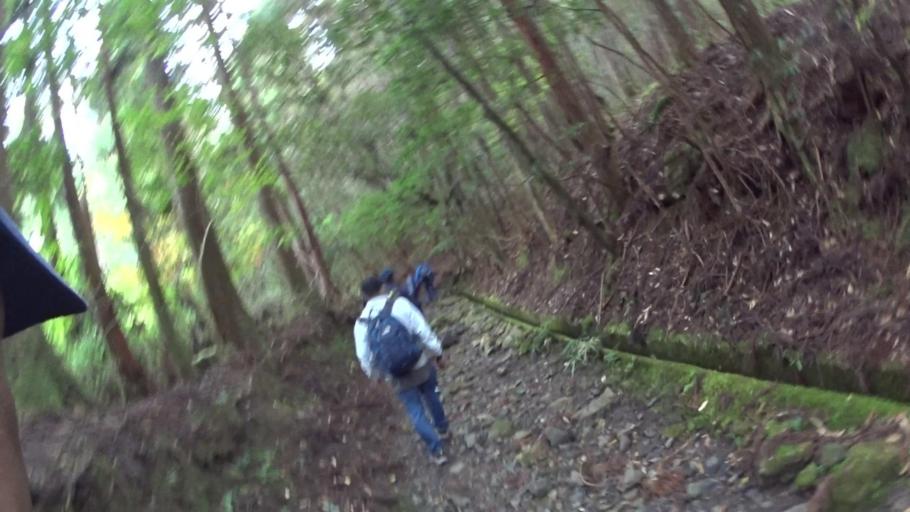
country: JP
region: Kyoto
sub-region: Kyoto-shi
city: Kamigyo-ku
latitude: 35.1126
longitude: 135.8117
